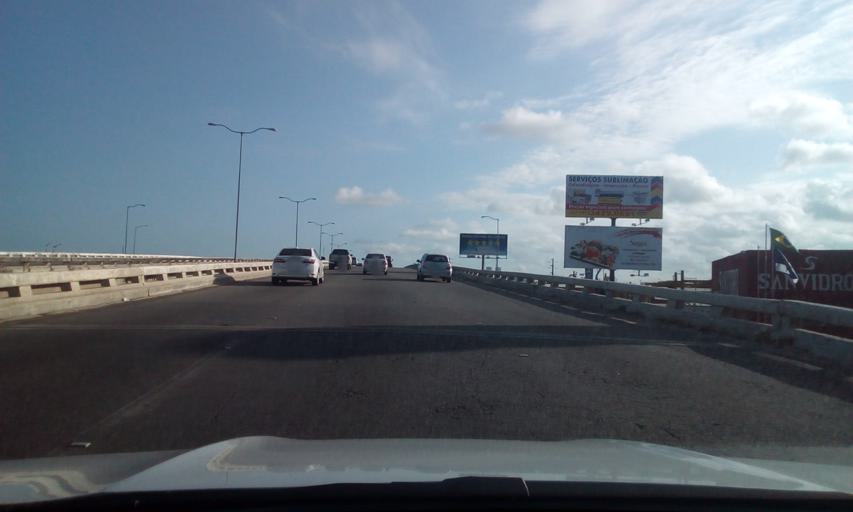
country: BR
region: Pernambuco
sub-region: Olinda
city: Olinda
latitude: -8.0170
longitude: -34.8604
